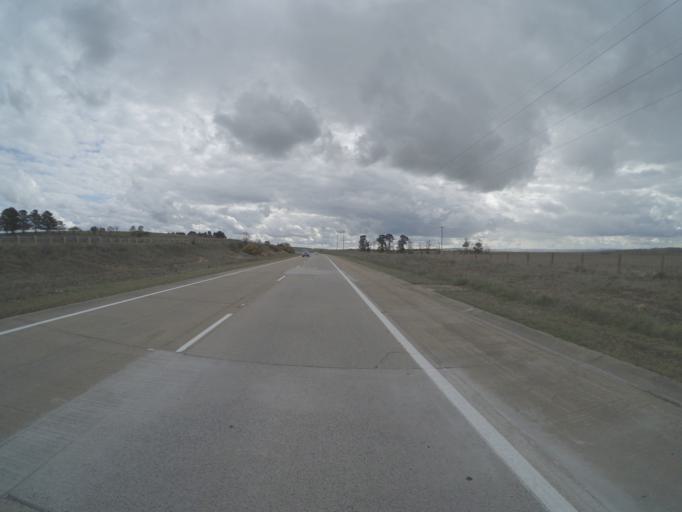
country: AU
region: New South Wales
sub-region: Goulburn Mulwaree
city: Goulburn
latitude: -34.8072
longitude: 149.5629
